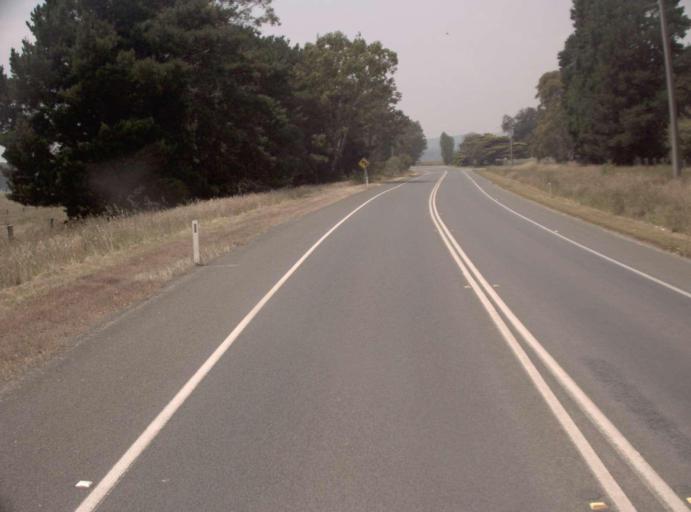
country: AU
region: Victoria
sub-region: Latrobe
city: Traralgon
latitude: -38.2428
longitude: 146.6339
